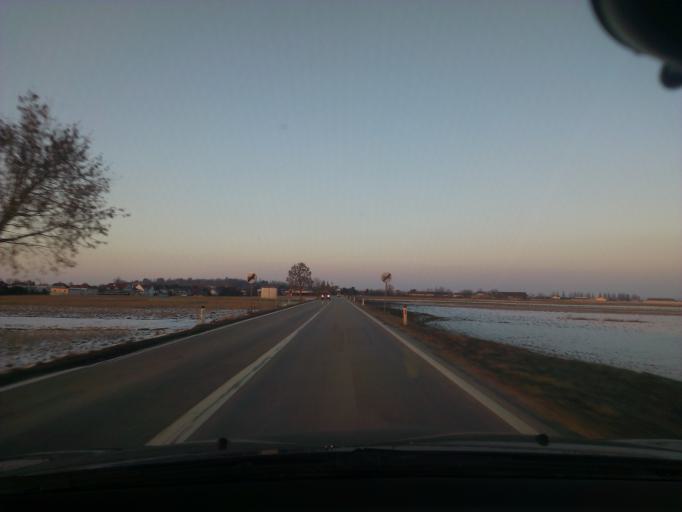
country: AT
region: Lower Austria
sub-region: Politischer Bezirk Baden
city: Reisenberg
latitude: 47.9864
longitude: 16.5170
